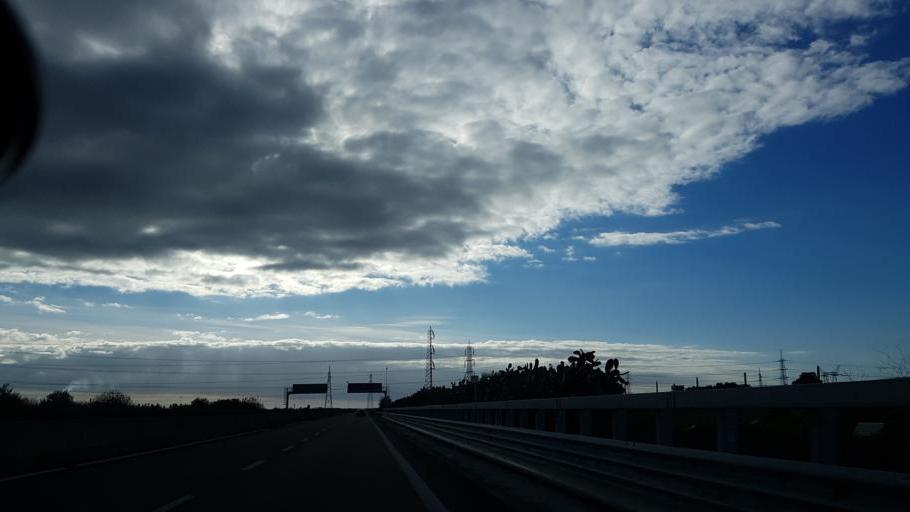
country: IT
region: Apulia
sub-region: Provincia di Brindisi
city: La Rosa
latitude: 40.6104
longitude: 17.9612
